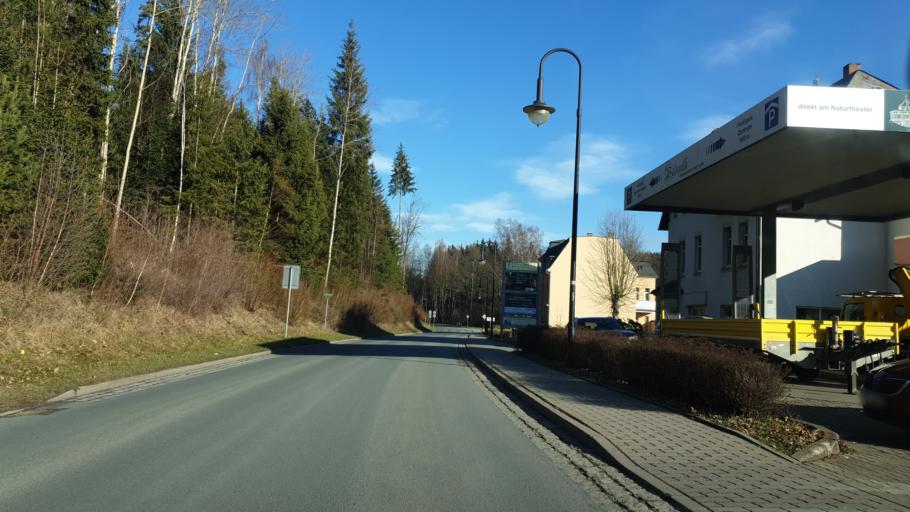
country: DE
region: Saxony
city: Bad Elster
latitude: 50.2893
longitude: 12.2414
